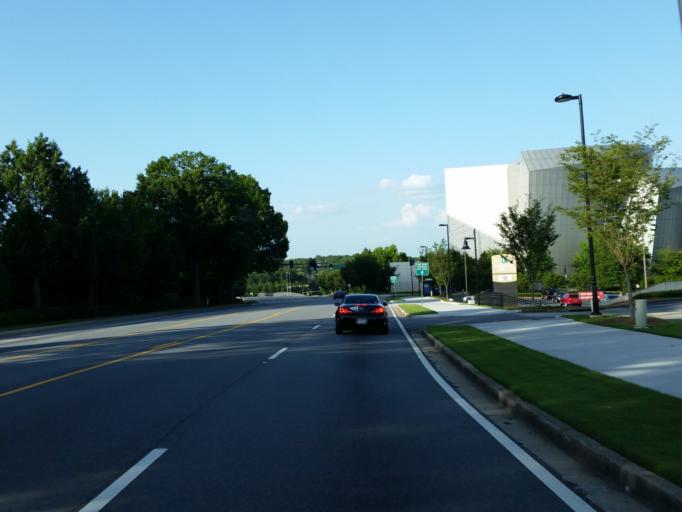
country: US
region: Georgia
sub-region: Cobb County
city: Vinings
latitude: 33.8840
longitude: -84.4612
